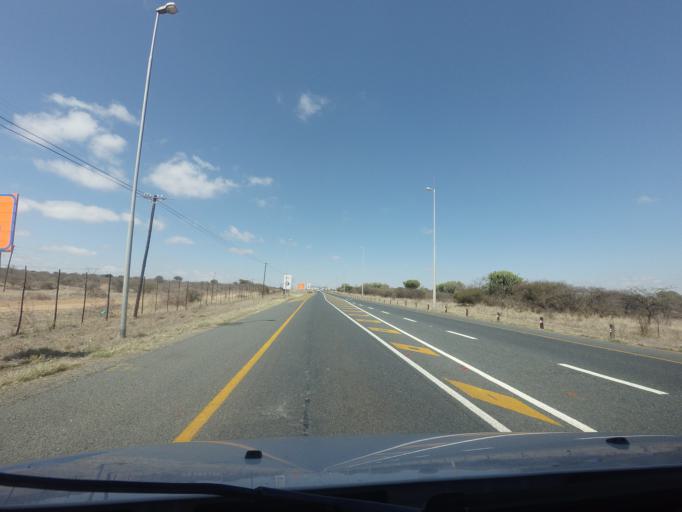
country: ZA
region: Limpopo
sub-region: Vhembe District Municipality
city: Louis Trichardt
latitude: -23.3631
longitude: 29.7783
